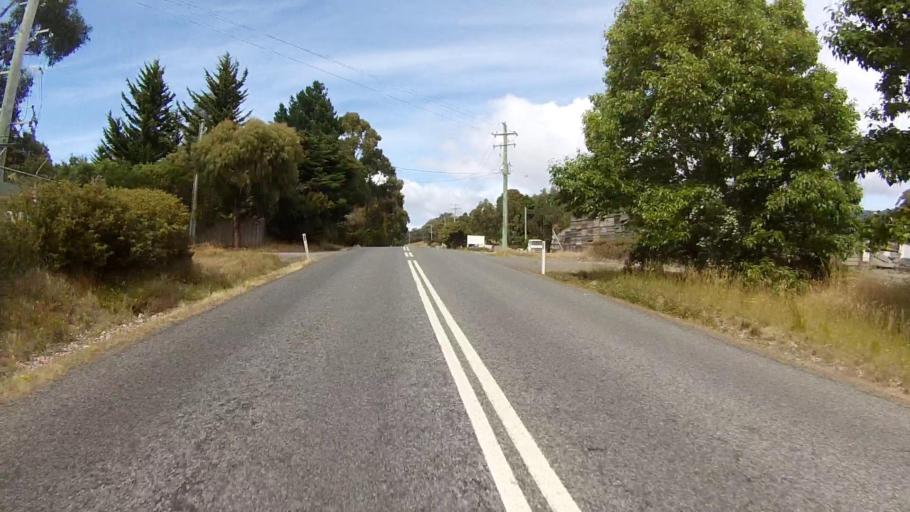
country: AU
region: Tasmania
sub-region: Kingborough
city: Kettering
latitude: -43.1379
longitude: 147.2456
